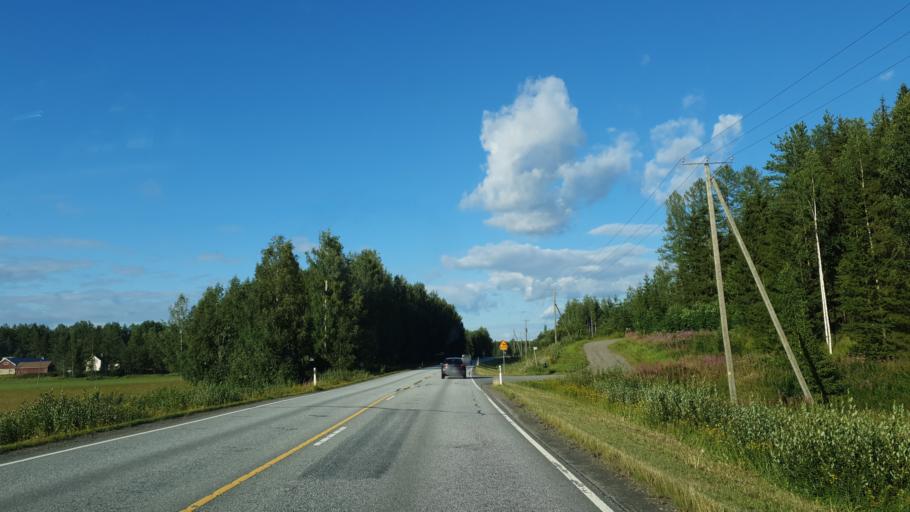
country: FI
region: North Karelia
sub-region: Joensuu
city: Outokumpu
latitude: 62.5695
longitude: 29.1556
